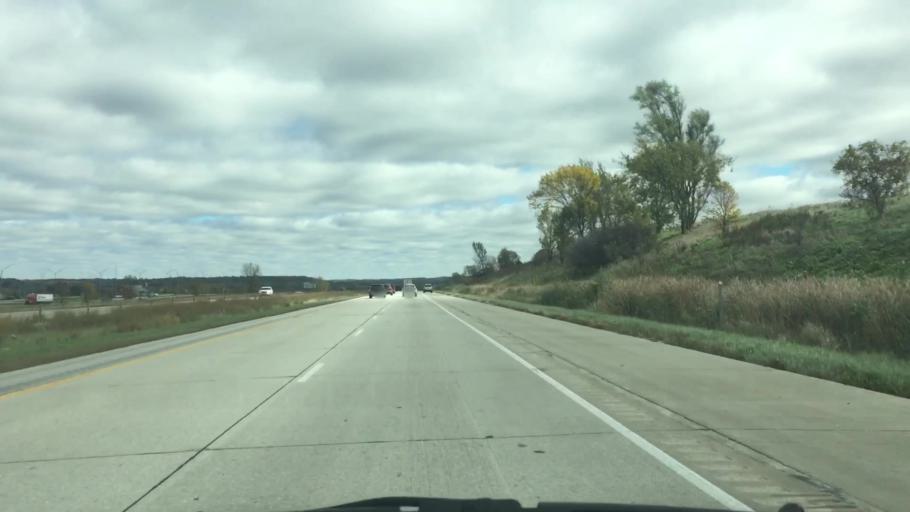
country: US
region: Iowa
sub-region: Polk County
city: Mitchellville
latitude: 41.6809
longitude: -93.3403
